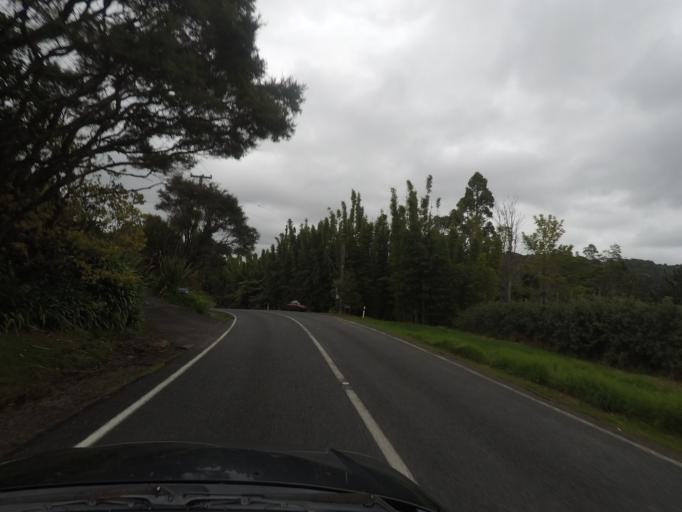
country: NZ
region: Auckland
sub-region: Auckland
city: Titirangi
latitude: -36.9287
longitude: 174.5941
